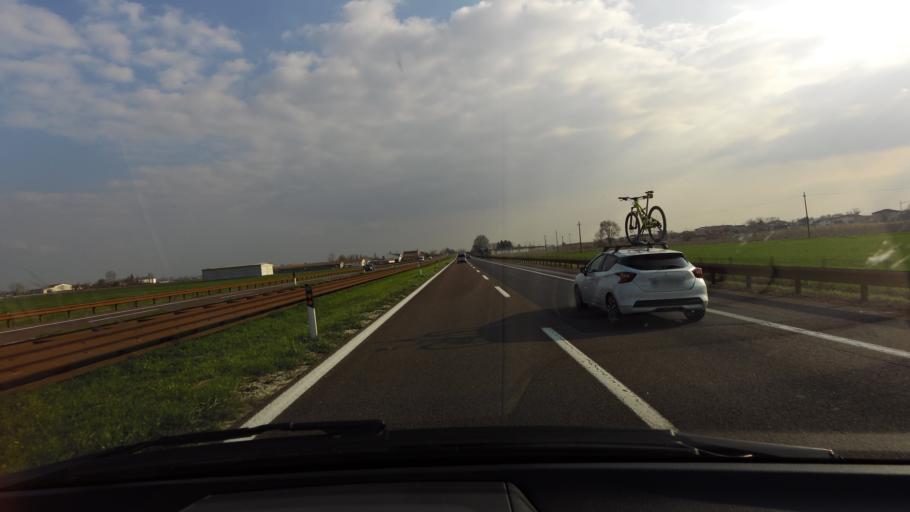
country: IT
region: Lombardy
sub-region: Provincia di Mantova
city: Bondeno
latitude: 44.9485
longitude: 10.8639
